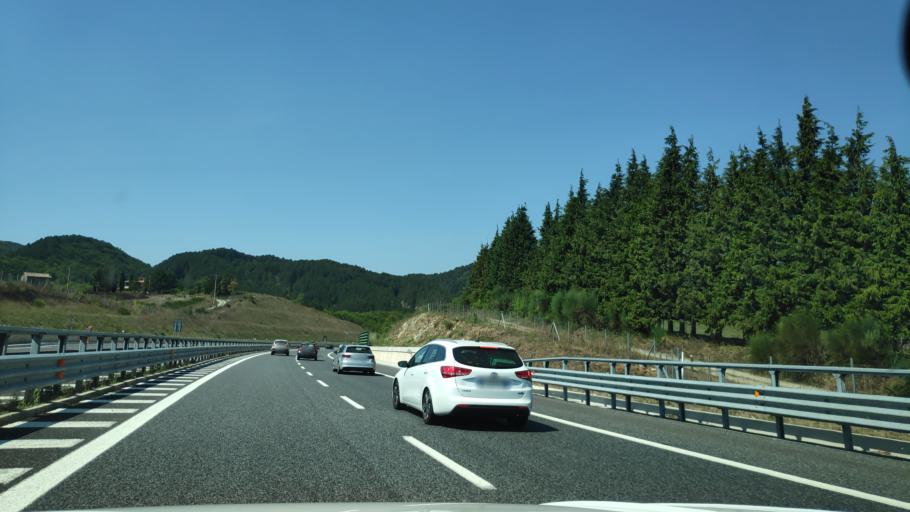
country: IT
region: Calabria
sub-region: Provincia di Cosenza
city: Mormanno
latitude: 39.8772
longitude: 15.9965
